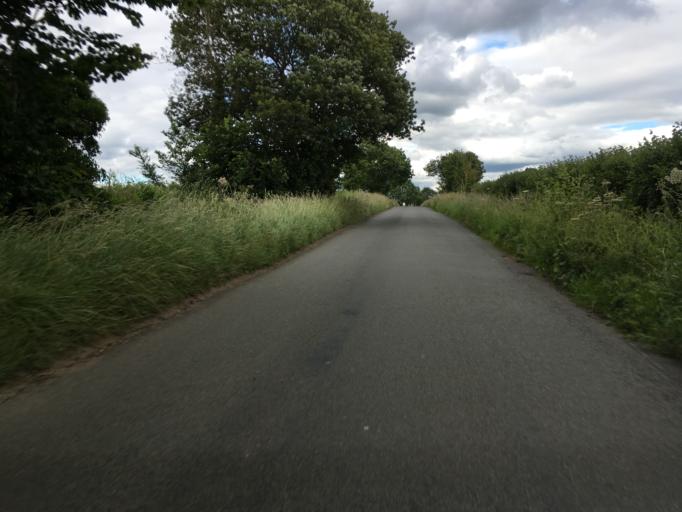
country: GB
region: England
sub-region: Oxfordshire
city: Boars Hill
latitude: 51.7029
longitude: -1.2724
